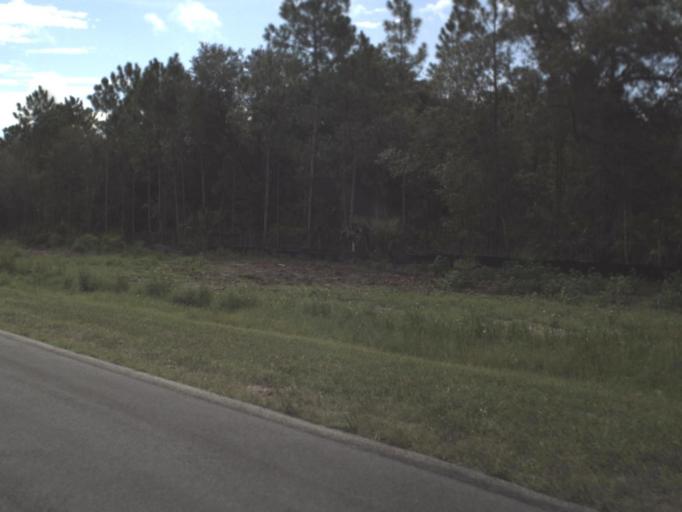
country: US
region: Florida
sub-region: Sarasota County
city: Plantation
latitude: 27.1119
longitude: -82.3311
